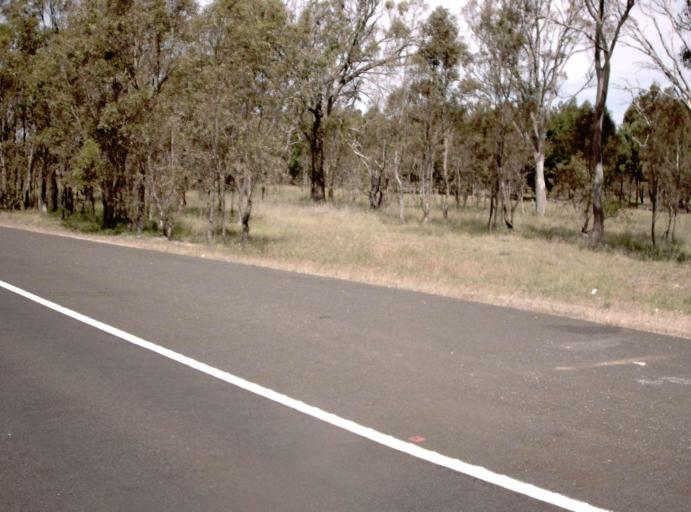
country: AU
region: Victoria
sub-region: East Gippsland
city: Bairnsdale
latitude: -37.8731
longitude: 147.4585
